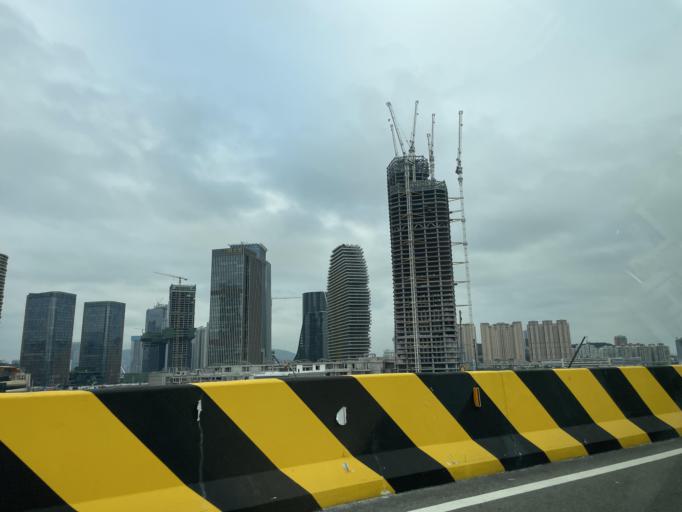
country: MO
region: Macau
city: Macau
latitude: 22.1414
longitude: 113.5463
